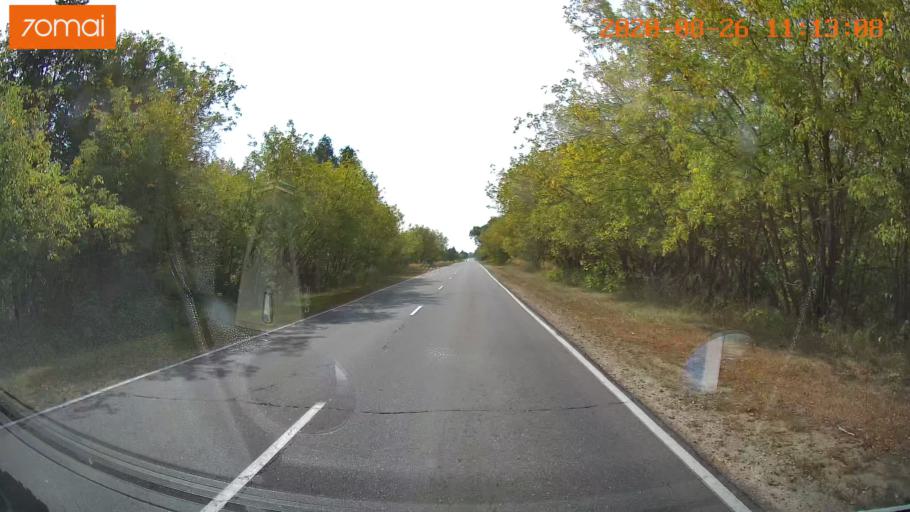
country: RU
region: Rjazan
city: Izhevskoye
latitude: 54.4619
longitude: 41.1224
